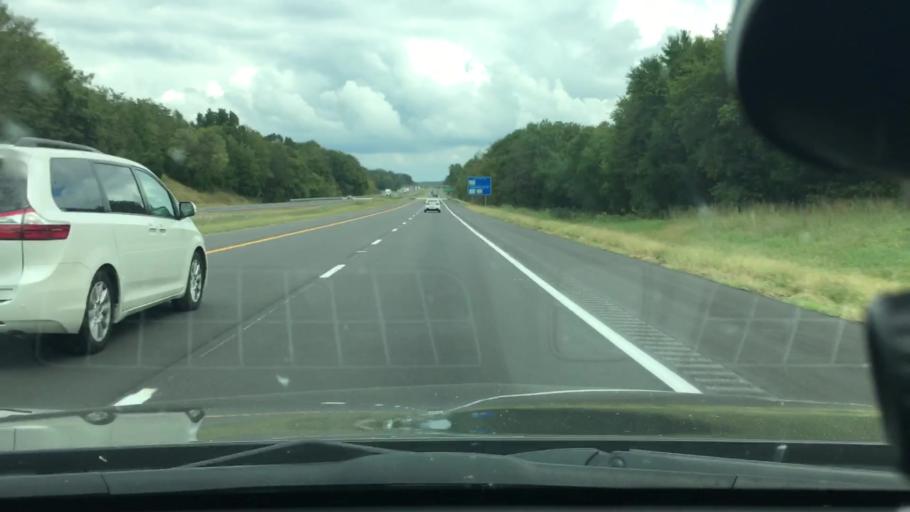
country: US
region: North Carolina
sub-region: Davie County
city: Mocksville
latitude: 35.9506
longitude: -80.5415
